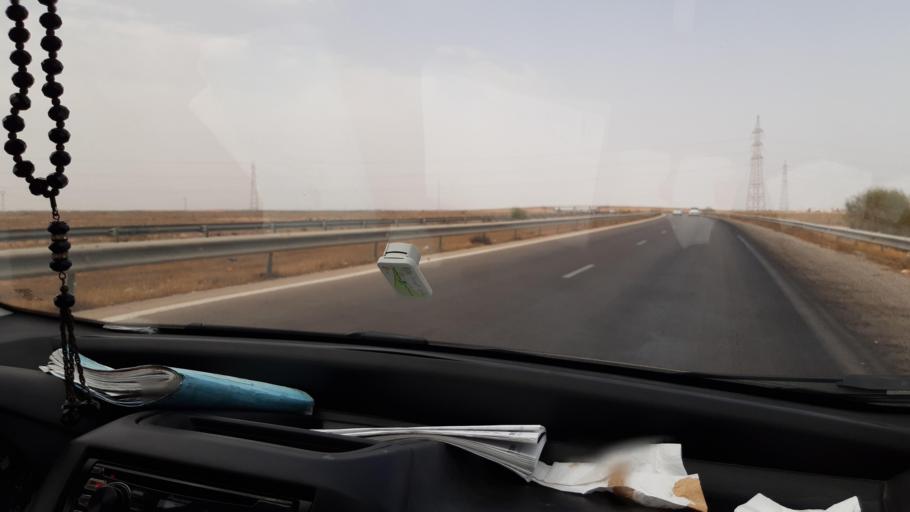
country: TN
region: Safaqis
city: Al Qarmadah
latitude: 34.9082
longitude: 10.7342
